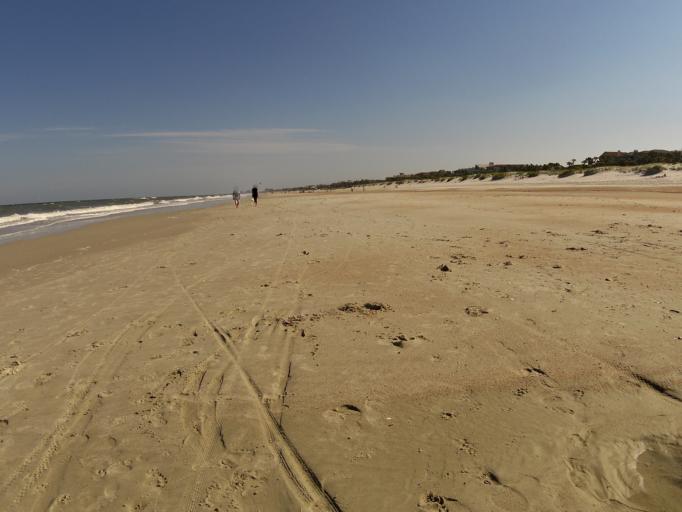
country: US
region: Florida
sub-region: Duval County
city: Atlantic Beach
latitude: 30.3597
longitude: -81.3970
